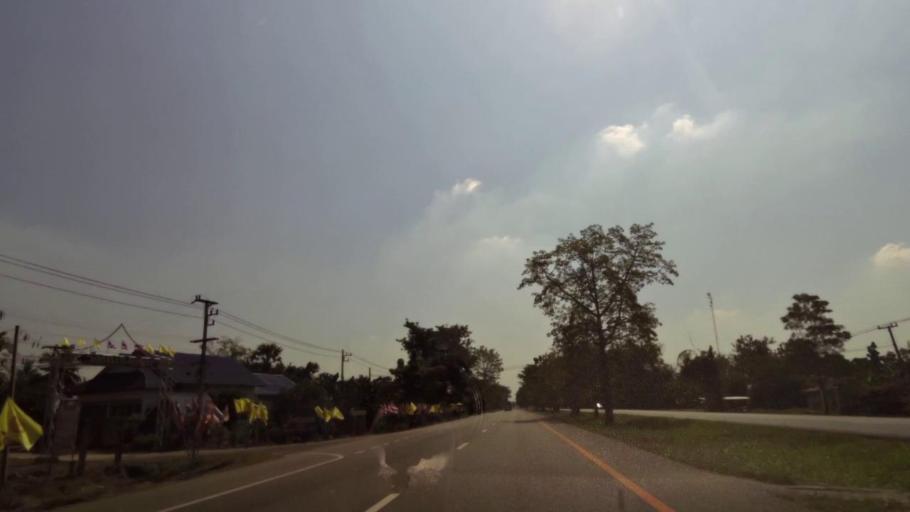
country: TH
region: Phichit
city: Bueng Na Rang
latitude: 16.2333
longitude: 100.1257
